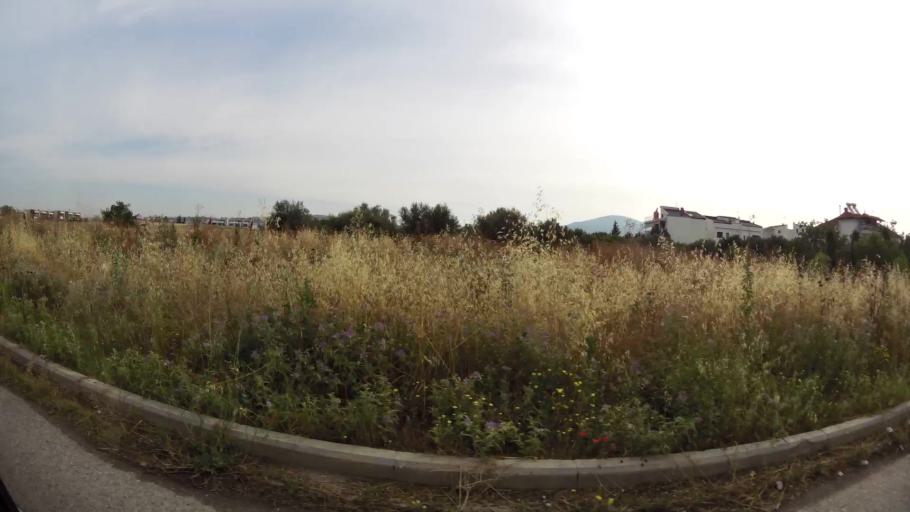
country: GR
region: Central Macedonia
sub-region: Nomos Thessalonikis
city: Thermi
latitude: 40.5487
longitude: 23.0117
